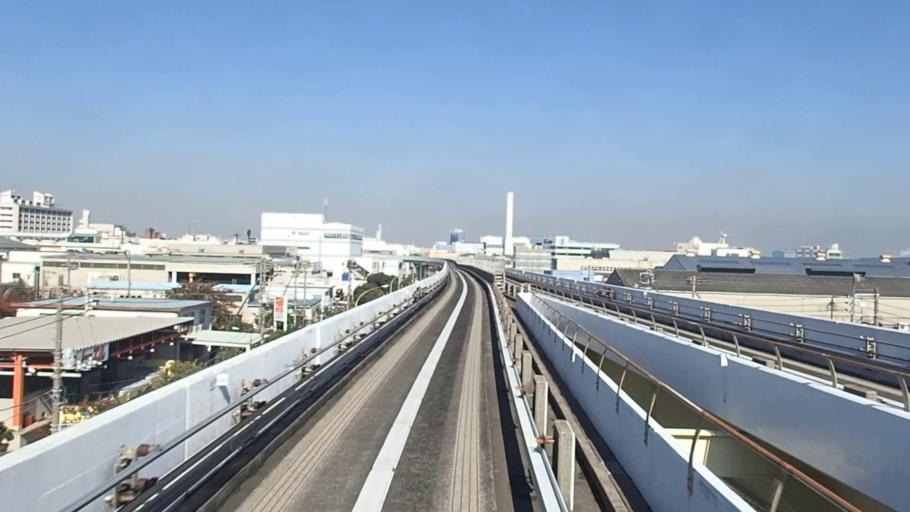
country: JP
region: Kanagawa
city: Yokosuka
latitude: 35.3501
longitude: 139.6485
